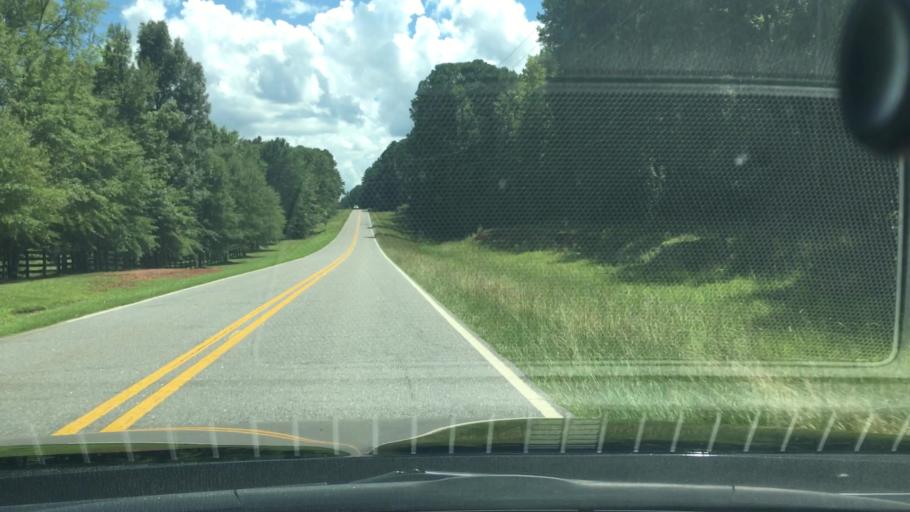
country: US
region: Georgia
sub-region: Putnam County
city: Jefferson
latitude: 33.3758
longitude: -83.2508
